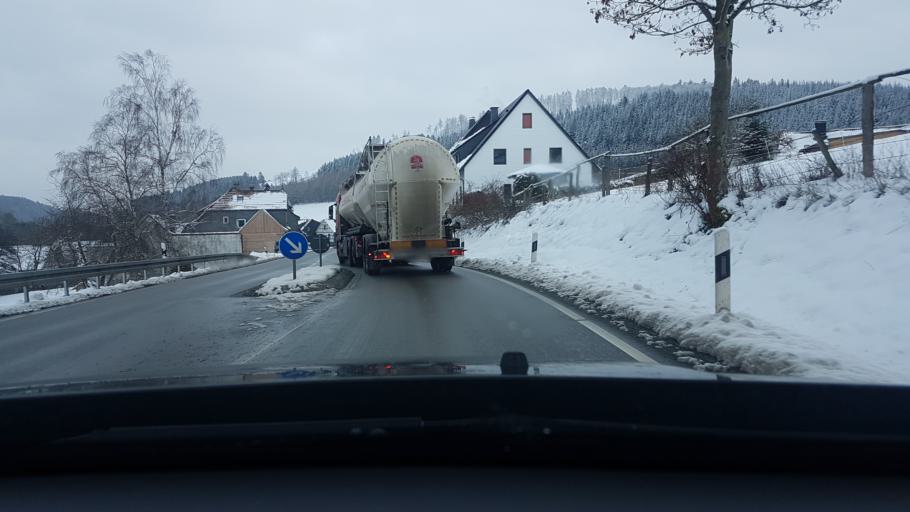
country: DE
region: North Rhine-Westphalia
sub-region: Regierungsbezirk Arnsberg
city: Medebach
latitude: 51.2934
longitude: 8.7267
